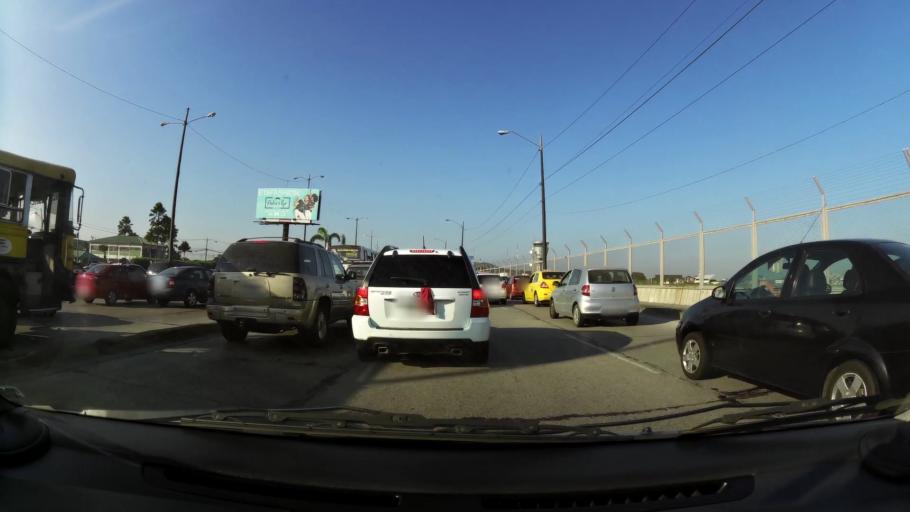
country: EC
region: Guayas
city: Eloy Alfaro
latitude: -2.1572
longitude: -79.8806
